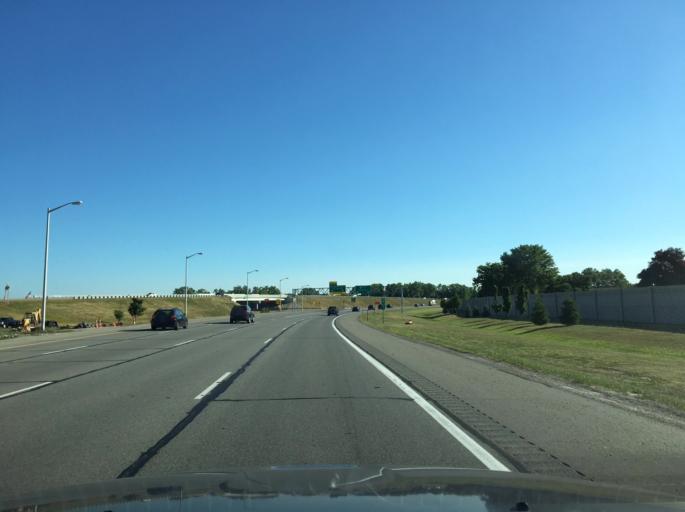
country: US
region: Michigan
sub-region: Macomb County
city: Sterling Heights
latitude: 42.5967
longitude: -83.0296
